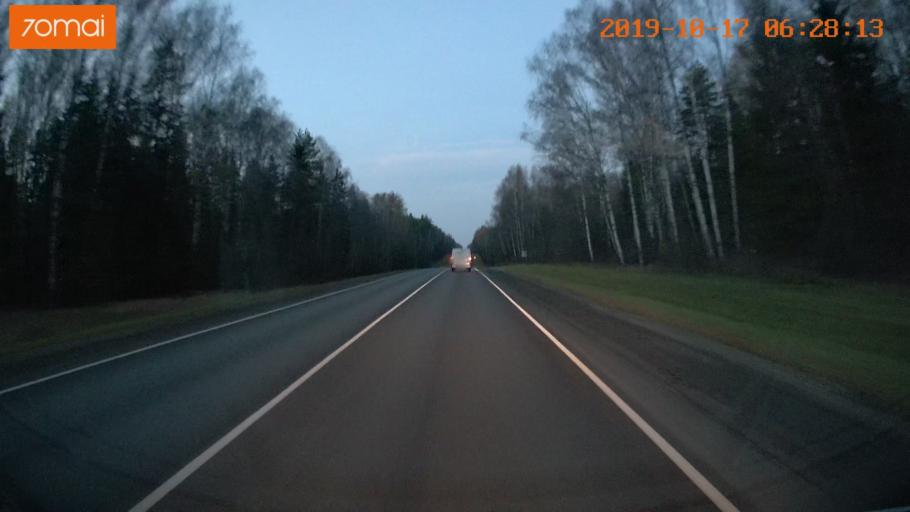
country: RU
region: Ivanovo
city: Lezhnevo
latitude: 56.7549
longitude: 40.7693
